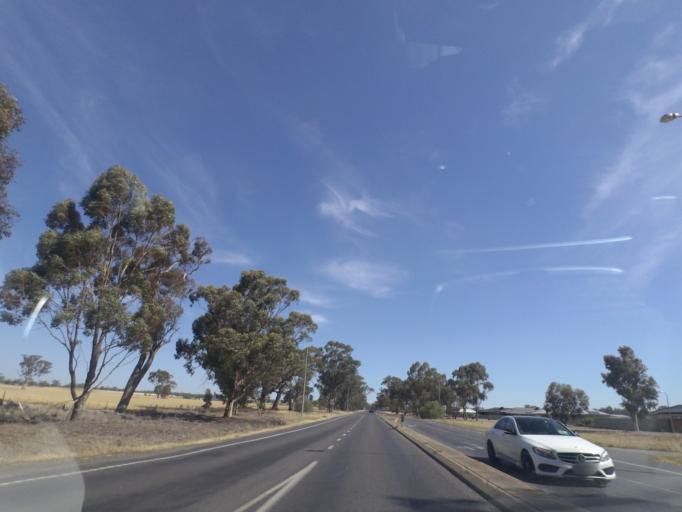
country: AU
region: Victoria
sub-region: Greater Shepparton
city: Shepparton
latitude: -36.4414
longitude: 145.3889
